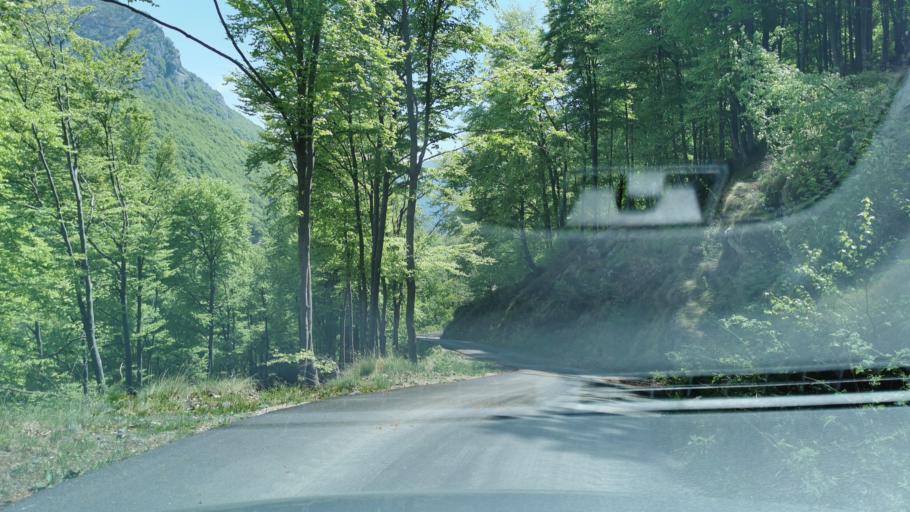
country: IT
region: Piedmont
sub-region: Provincia di Torino
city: Lemie
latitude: 45.2395
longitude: 7.2823
